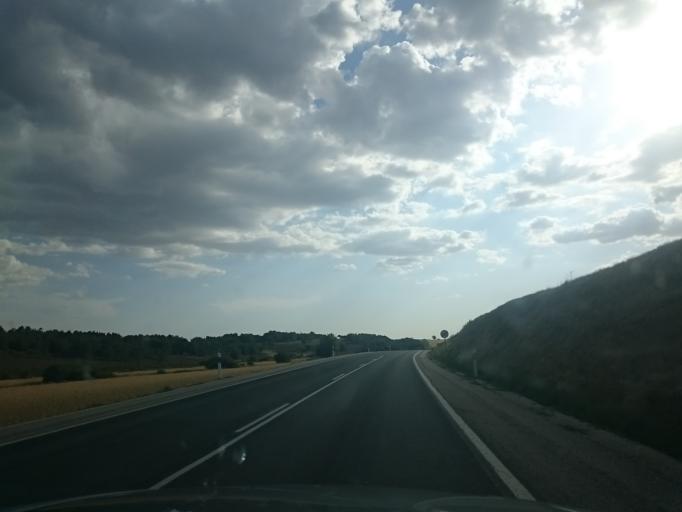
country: ES
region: Castille and Leon
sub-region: Provincia de Burgos
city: Atapuerca
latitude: 42.3419
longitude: -3.4997
